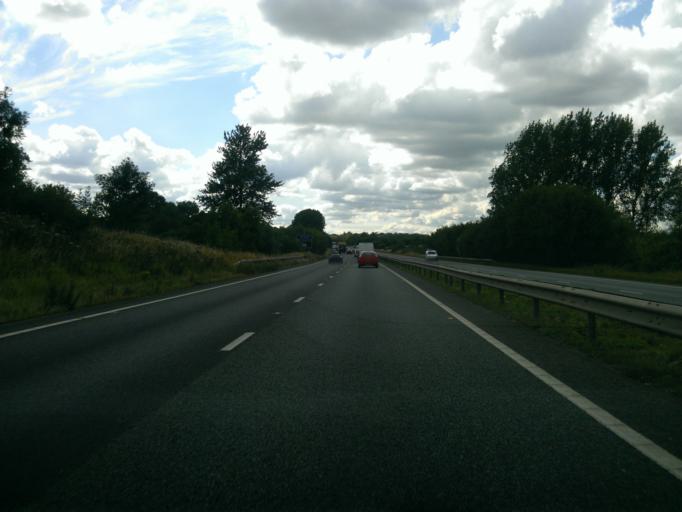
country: GB
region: England
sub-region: Northamptonshire
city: Long Buckby
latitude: 52.3983
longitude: -1.0192
